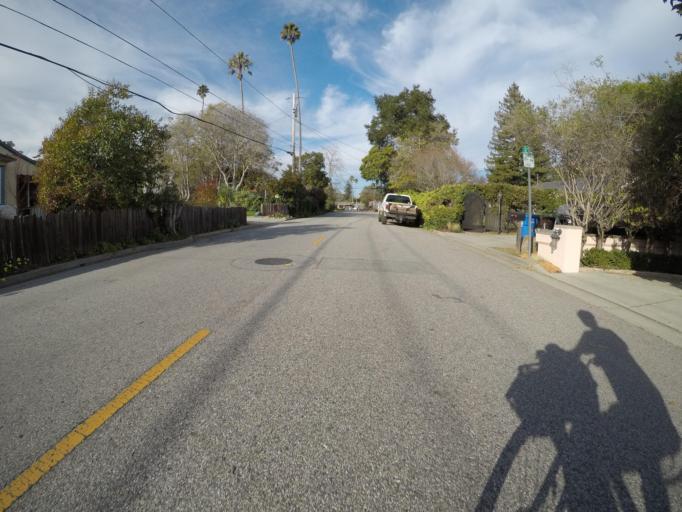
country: US
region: California
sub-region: Santa Cruz County
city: Santa Cruz
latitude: 36.9770
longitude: -122.0427
